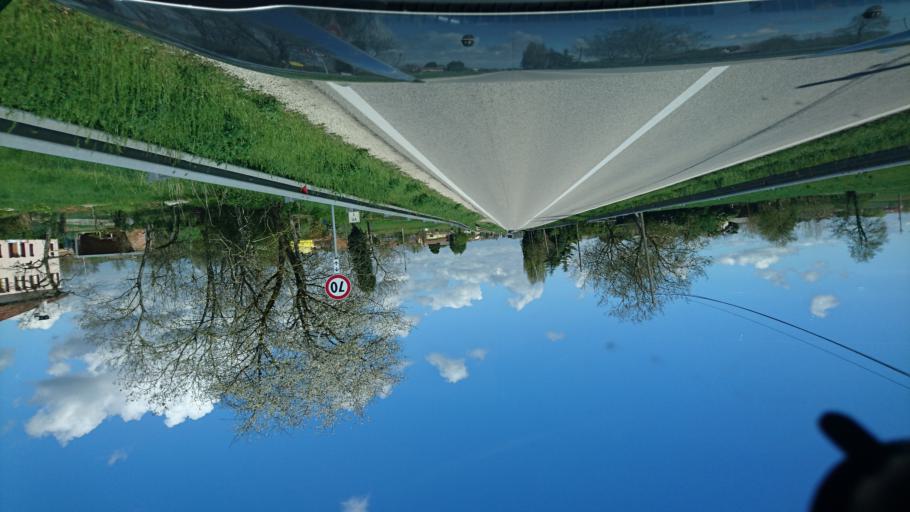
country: IT
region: Veneto
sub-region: Provincia di Padova
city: Saletto
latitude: 45.4855
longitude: 11.8826
